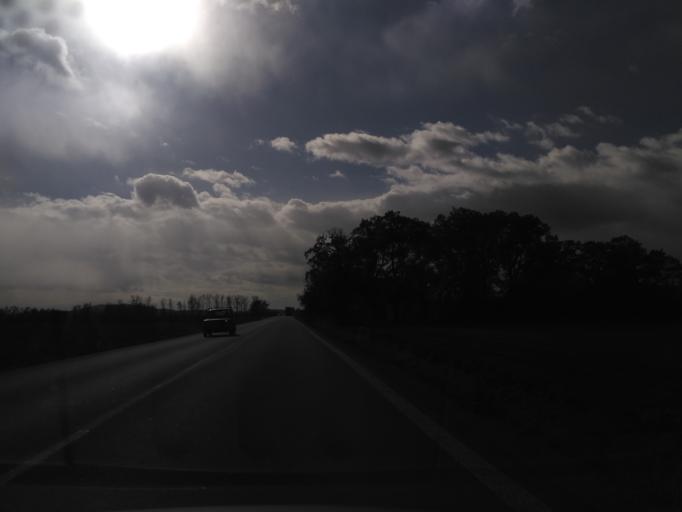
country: SK
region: Kosicky
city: Trebisov
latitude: 48.5932
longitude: 21.7118
